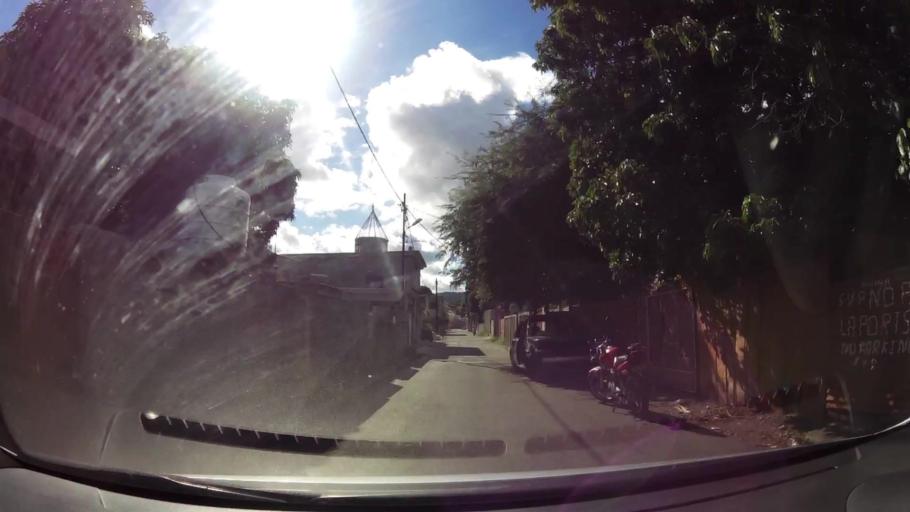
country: MU
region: Pamplemousses
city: Le Hochet
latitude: -20.1482
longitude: 57.5167
